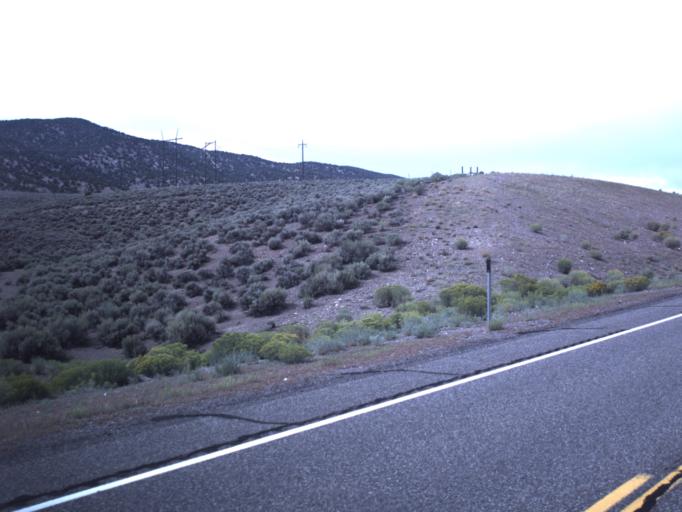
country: US
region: Utah
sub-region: Piute County
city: Junction
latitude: 38.3086
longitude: -112.2227
